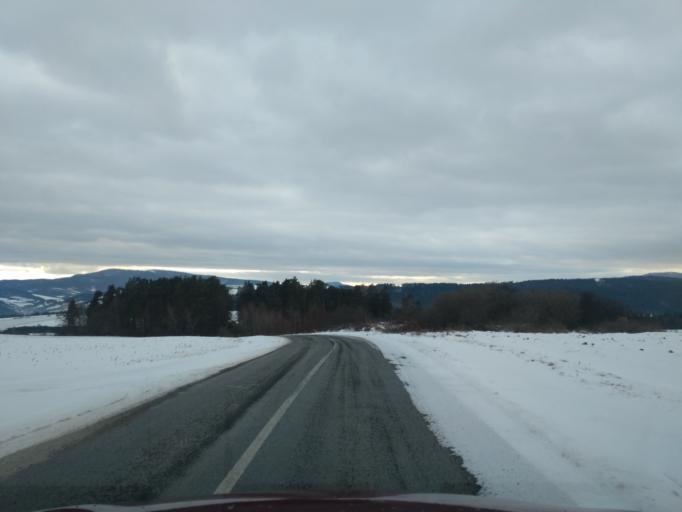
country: SK
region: Presovsky
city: Sabinov
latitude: 49.0307
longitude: 21.0617
